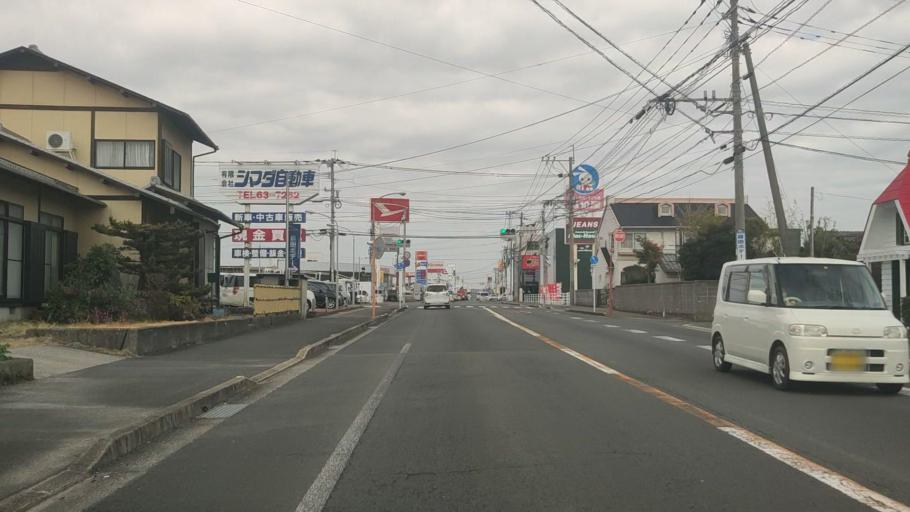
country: JP
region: Nagasaki
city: Shimabara
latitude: 32.8038
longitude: 130.3630
